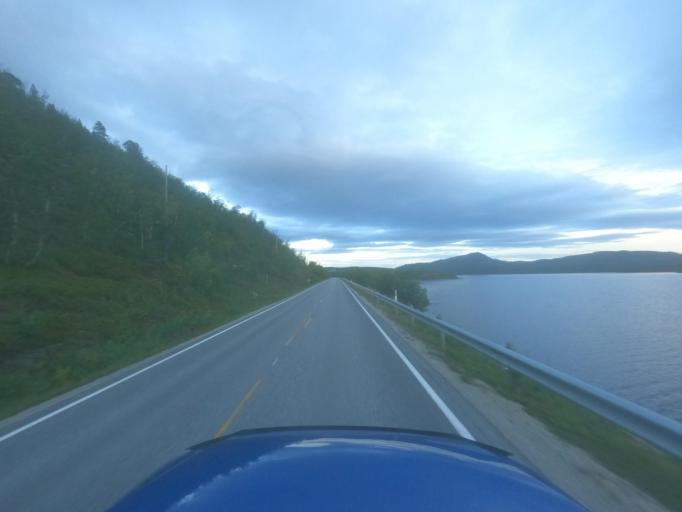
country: NO
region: Finnmark Fylke
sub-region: Porsanger
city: Lakselv
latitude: 69.9160
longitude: 24.9819
